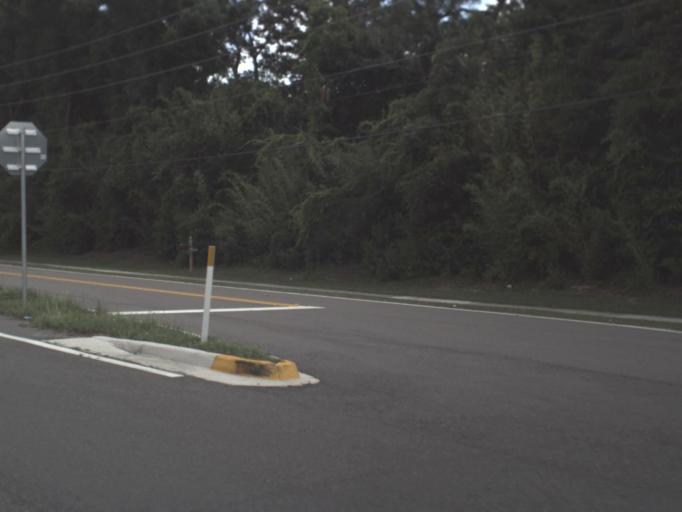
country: US
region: Florida
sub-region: Duval County
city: Jacksonville
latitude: 30.3111
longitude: -81.5587
